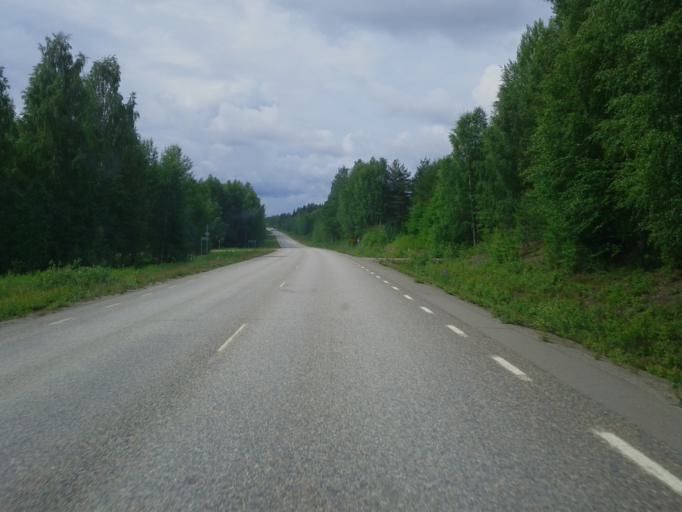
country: SE
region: Vaesterbotten
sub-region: Norsjo Kommun
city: Norsjoe
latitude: 64.9765
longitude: 19.6967
